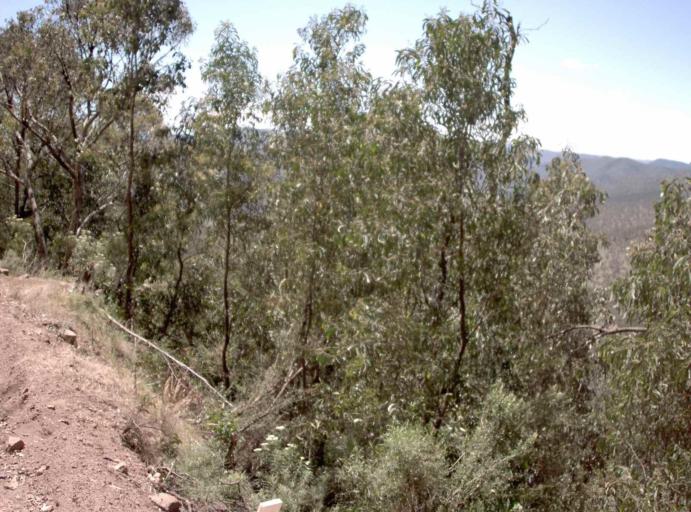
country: AU
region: New South Wales
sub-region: Snowy River
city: Jindabyne
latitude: -36.9859
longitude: 148.3004
